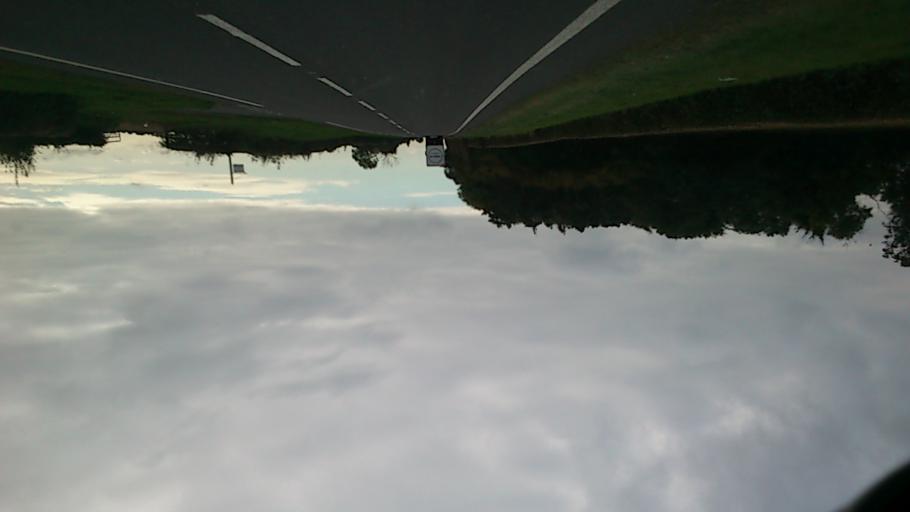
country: GB
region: England
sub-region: Shropshire
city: Westbury
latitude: 52.7069
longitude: -2.9112
